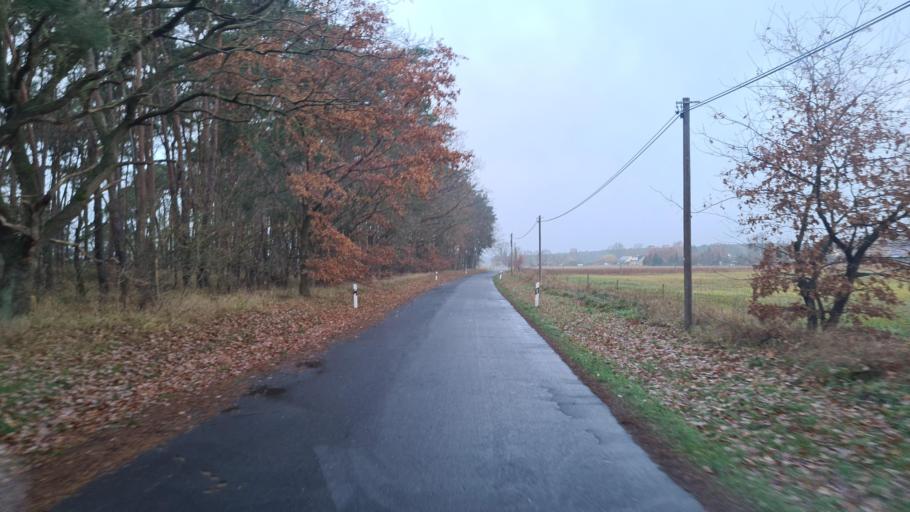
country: DE
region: Brandenburg
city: Borkheide
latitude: 52.1851
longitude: 12.9110
